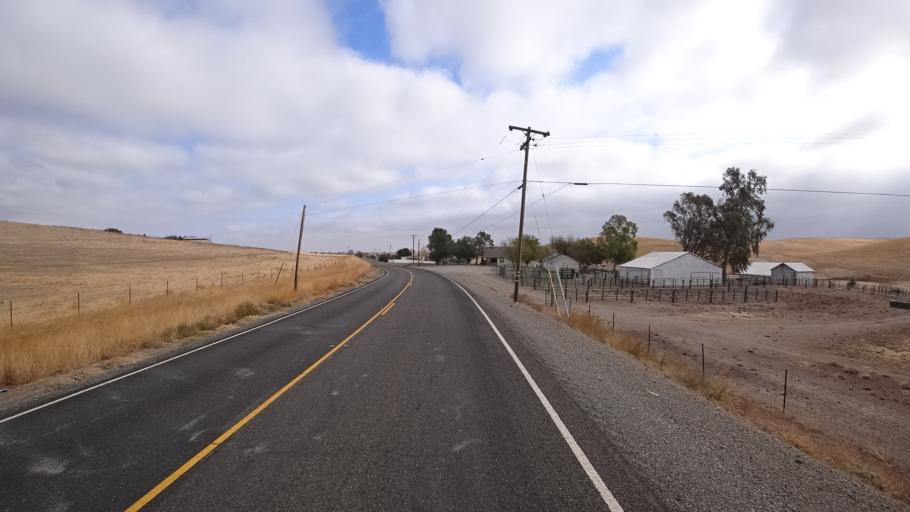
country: US
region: California
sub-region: Yolo County
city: Dunnigan
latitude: 38.7844
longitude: -121.9240
